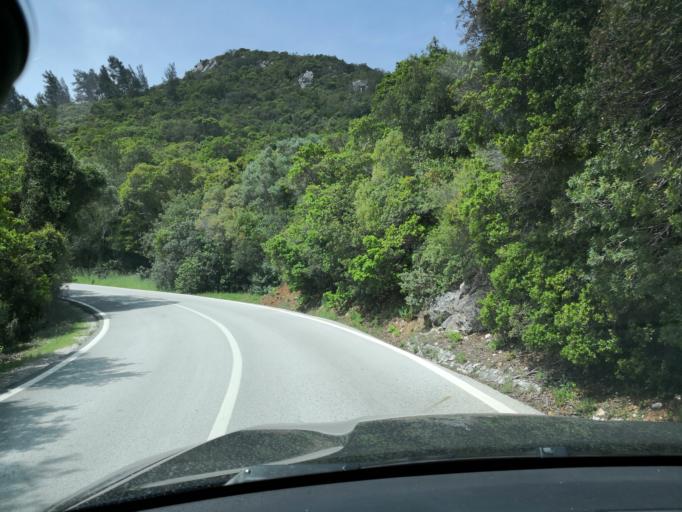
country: PT
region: Setubal
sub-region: Sesimbra
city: Sesimbra
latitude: 38.4699
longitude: -8.9942
